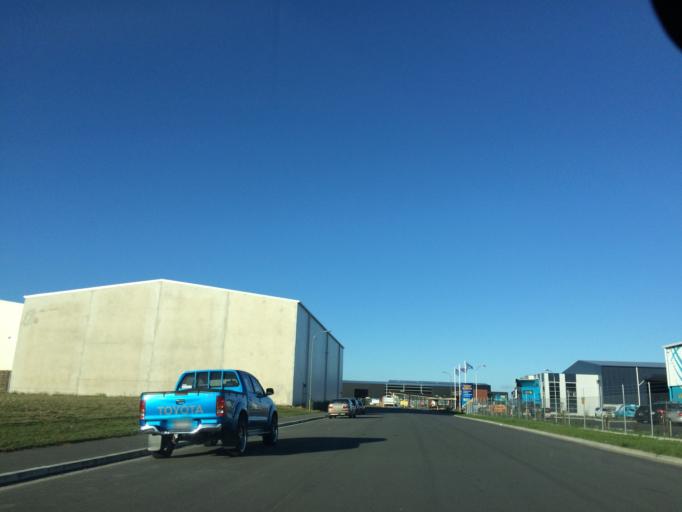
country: NZ
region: Canterbury
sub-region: Selwyn District
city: Prebbleton
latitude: -43.5398
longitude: 172.5461
